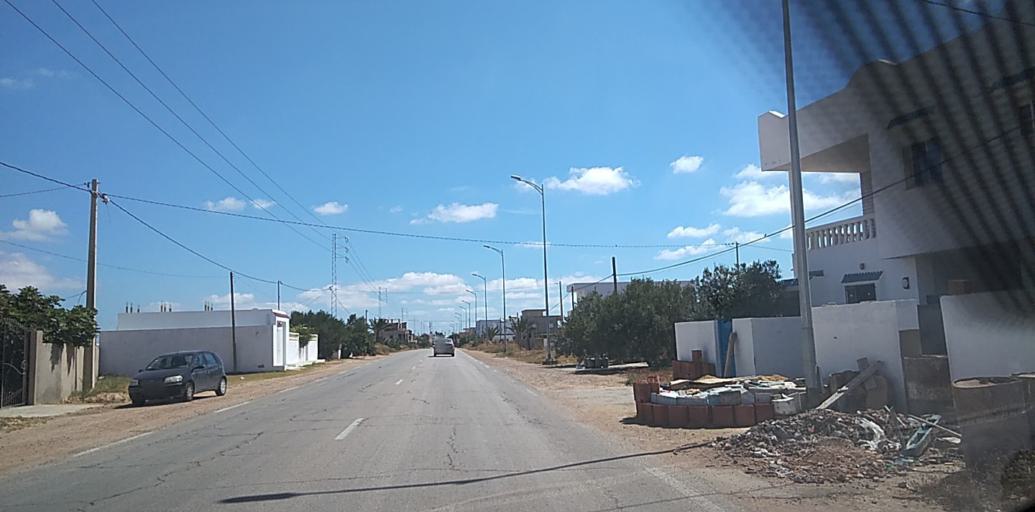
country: TN
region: Safaqis
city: Al Qarmadah
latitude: 34.6682
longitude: 11.1333
